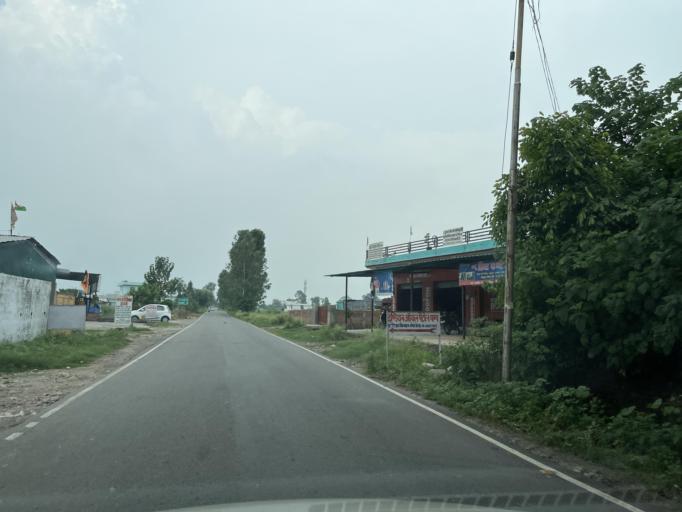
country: IN
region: Uttarakhand
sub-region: Naini Tal
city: Haldwani
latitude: 29.1751
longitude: 79.4702
